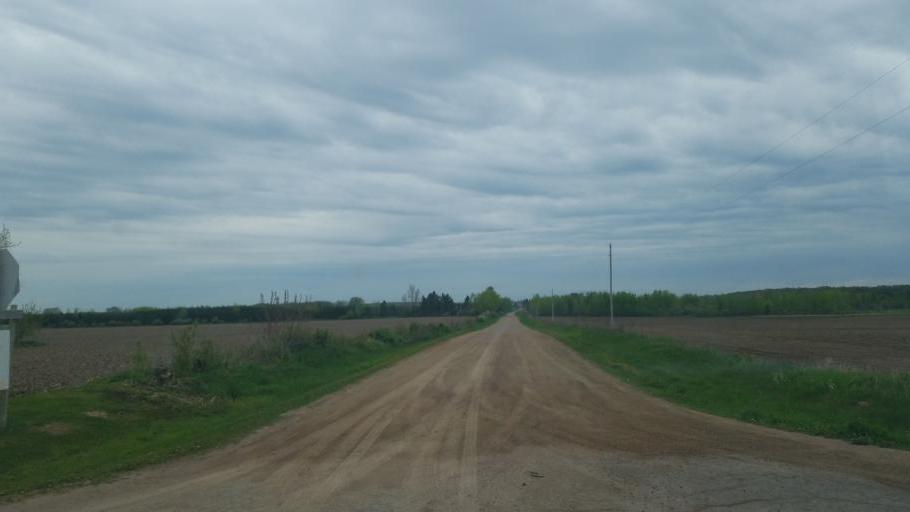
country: US
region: Wisconsin
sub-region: Clark County
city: Loyal
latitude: 44.6541
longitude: -90.4177
